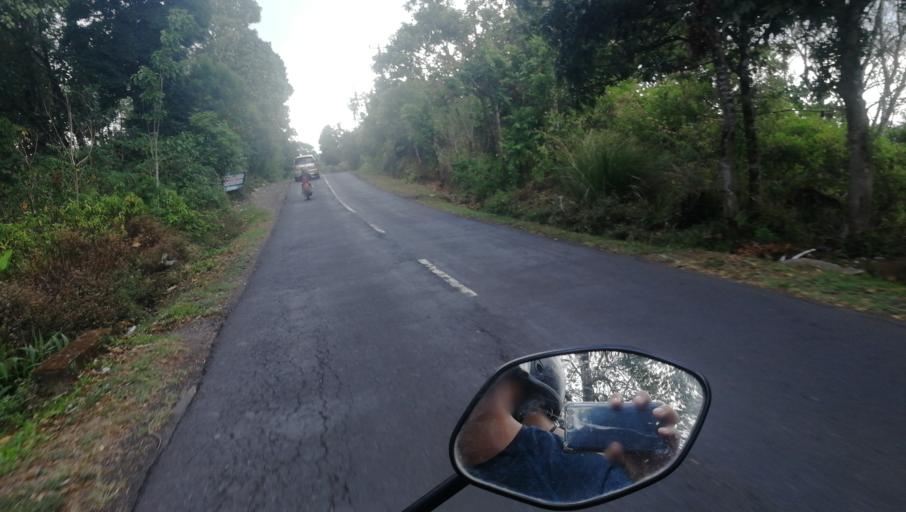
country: ID
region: Bali
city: Munduk
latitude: -8.2479
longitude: 115.0977
